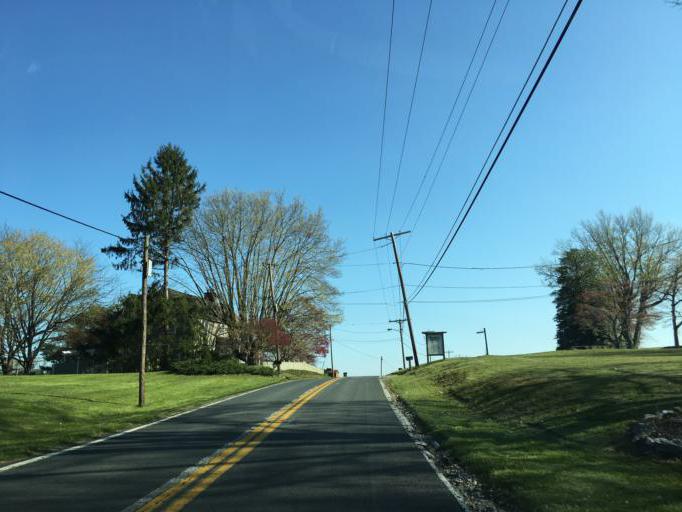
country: US
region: Maryland
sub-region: Baltimore County
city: Perry Hall
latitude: 39.4494
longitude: -76.4959
